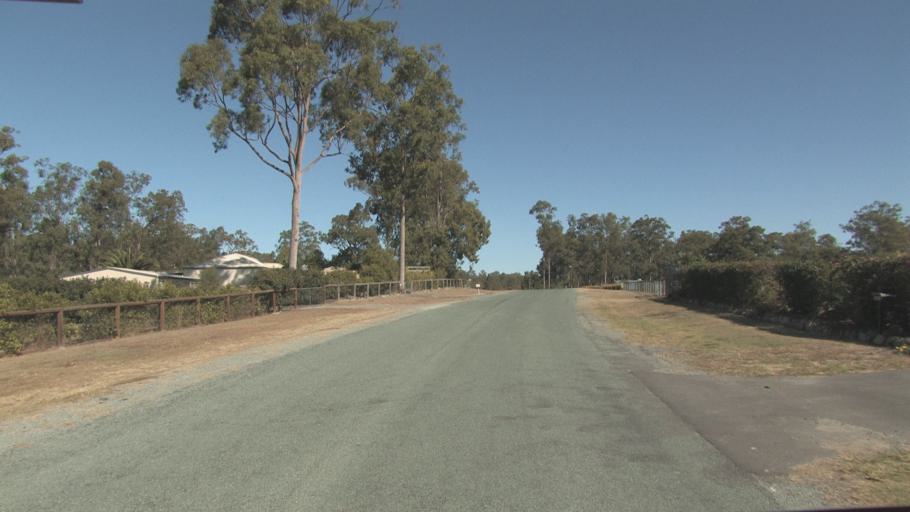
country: AU
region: Queensland
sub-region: Logan
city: Cedar Vale
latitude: -27.8637
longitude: 153.0338
